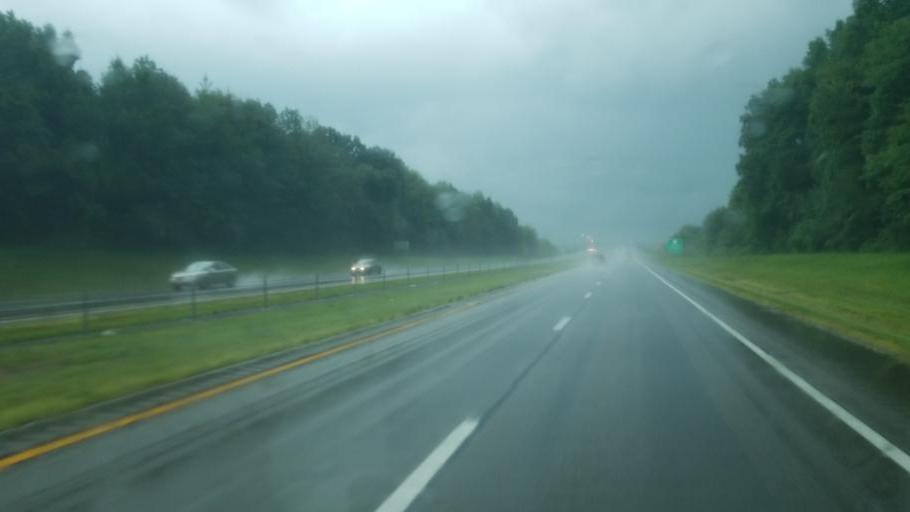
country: US
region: Ohio
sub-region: Trumbull County
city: Morgandale
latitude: 41.2760
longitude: -80.7885
